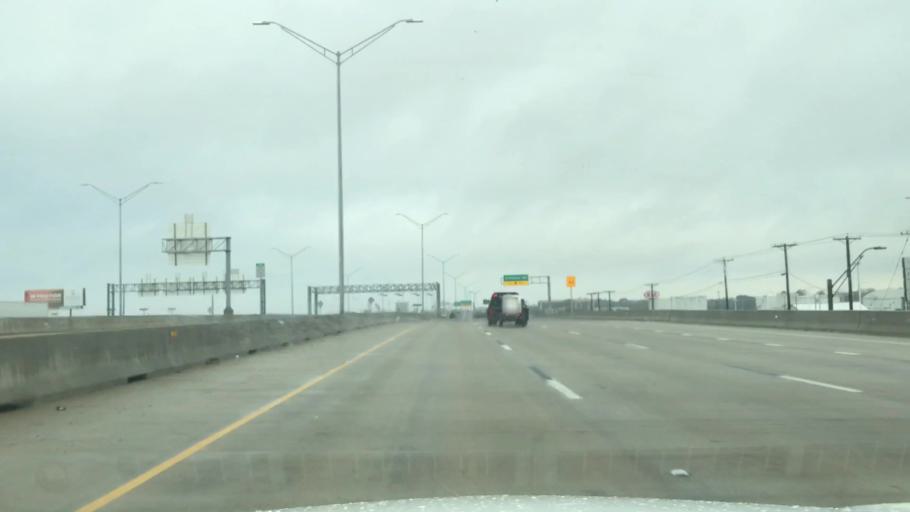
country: US
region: Texas
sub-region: Dallas County
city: Irving
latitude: 32.8375
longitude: -96.9300
